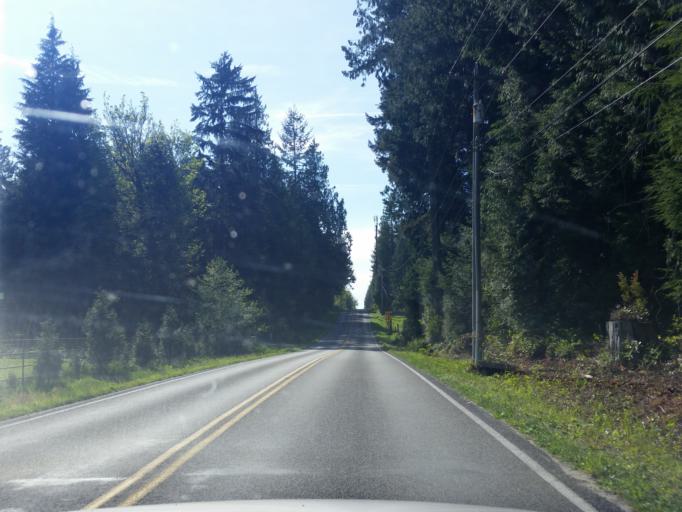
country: US
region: Washington
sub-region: Snohomish County
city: Three Lakes
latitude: 47.9633
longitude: -122.0041
